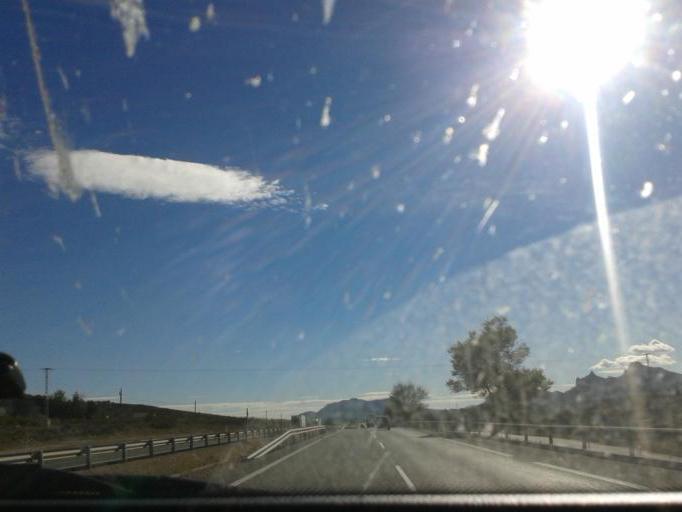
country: ES
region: Valencia
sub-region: Provincia de Alicante
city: Villena
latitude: 38.5901
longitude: -0.8443
